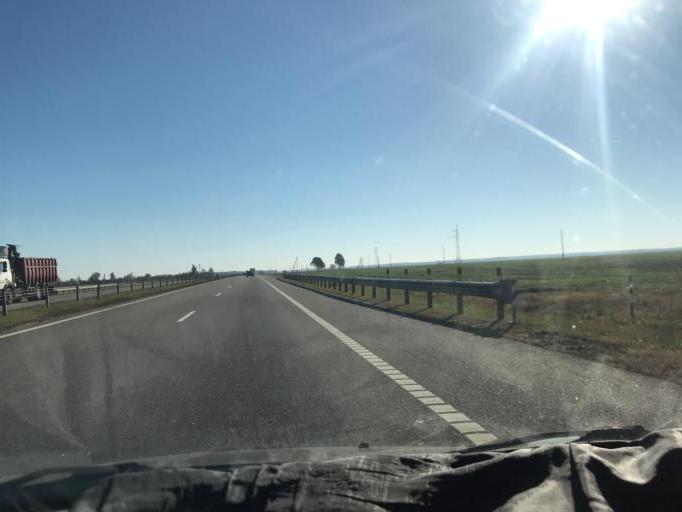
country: BY
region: Mogilev
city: Yalizava
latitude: 53.2377
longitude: 28.9659
